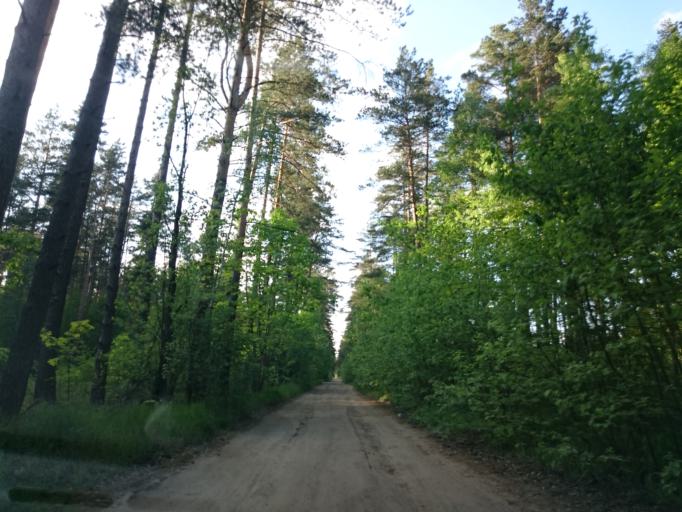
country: LV
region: Stopini
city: Ulbroka
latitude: 56.9465
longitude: 24.2887
